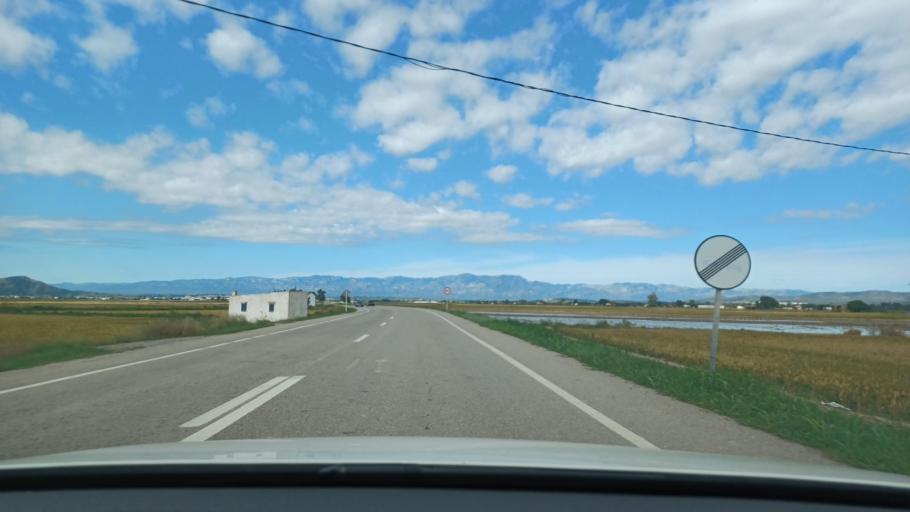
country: ES
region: Catalonia
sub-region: Provincia de Tarragona
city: Deltebre
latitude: 40.7016
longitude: 0.6727
